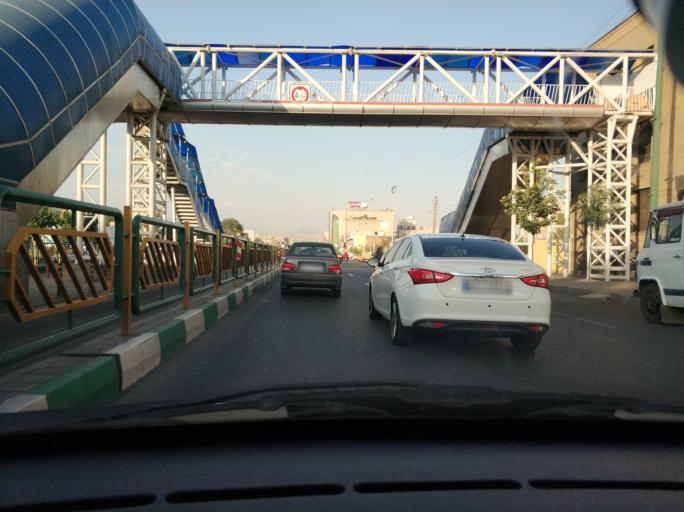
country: IR
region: Tehran
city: Tehran
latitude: 35.7072
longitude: 51.4667
